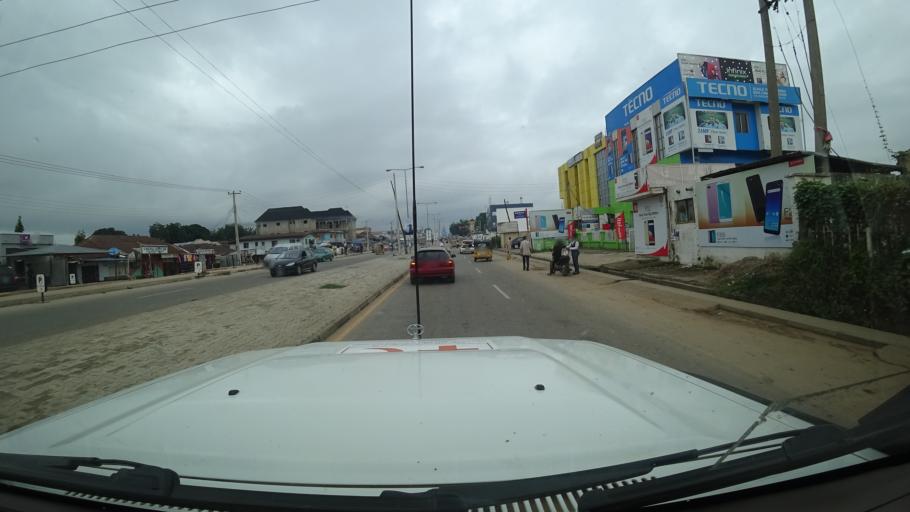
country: NG
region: Niger
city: Minna
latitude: 9.6156
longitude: 6.5470
